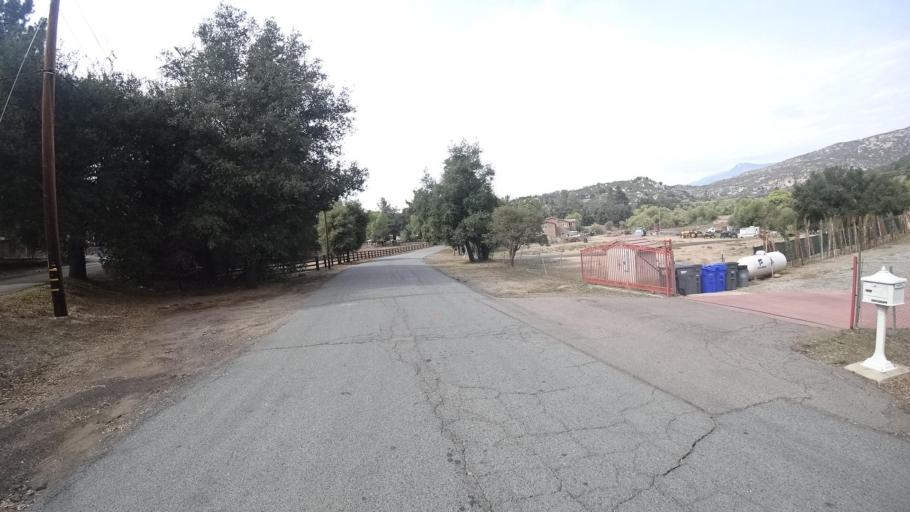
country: US
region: California
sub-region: San Diego County
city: Descanso
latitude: 32.8634
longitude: -116.6242
